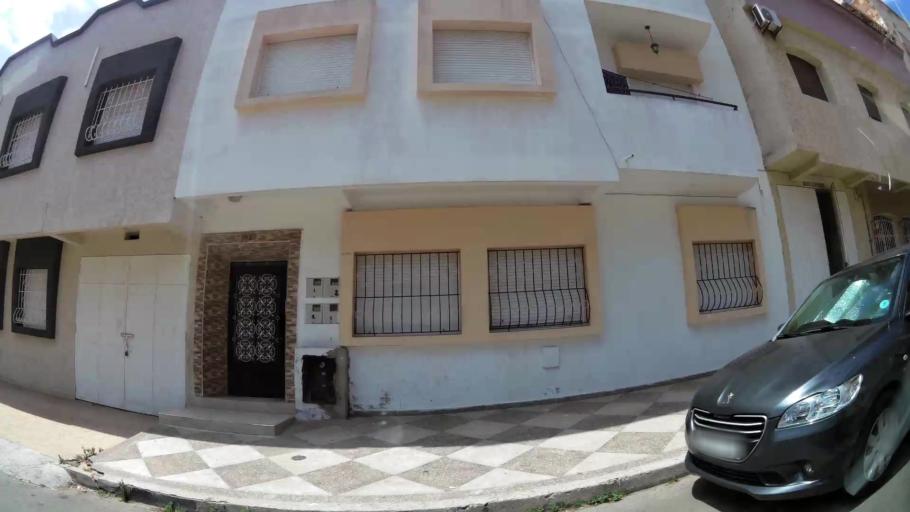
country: MA
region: Gharb-Chrarda-Beni Hssen
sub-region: Kenitra Province
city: Kenitra
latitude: 34.2740
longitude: -6.6039
